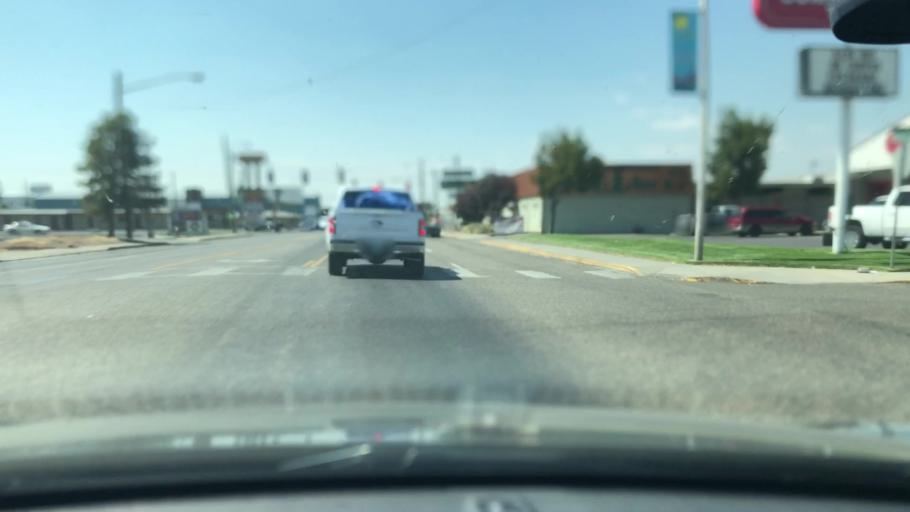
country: US
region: Oregon
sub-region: Malheur County
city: Ontario
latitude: 44.0258
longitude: -116.9574
